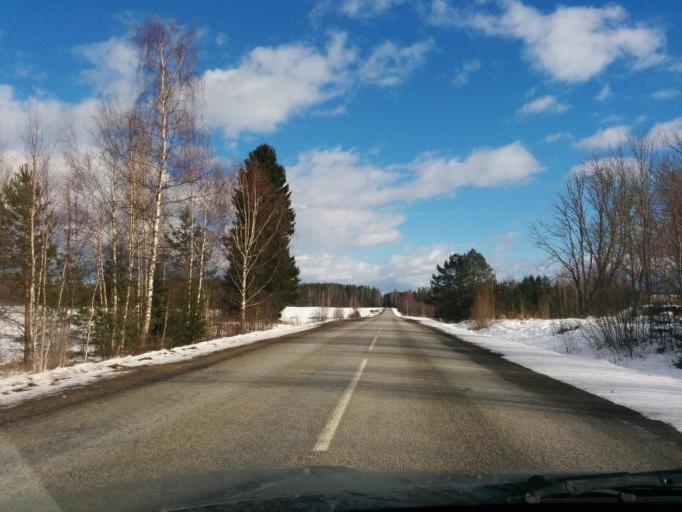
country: LV
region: Gulbenes Rajons
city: Gulbene
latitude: 57.1928
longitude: 26.9825
